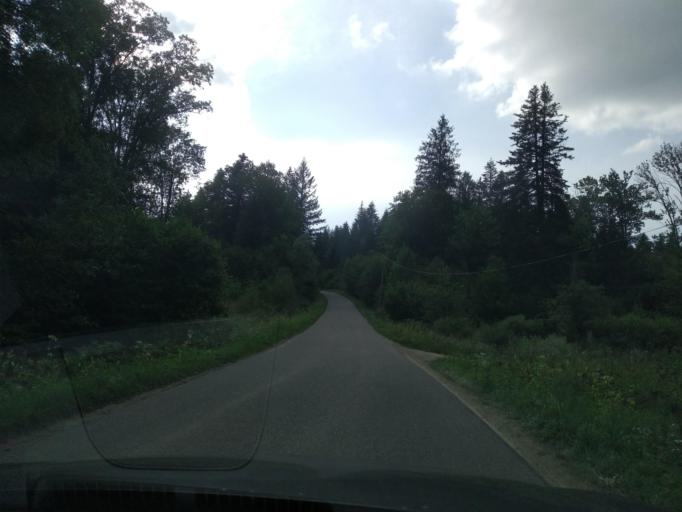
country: PL
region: Subcarpathian Voivodeship
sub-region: Powiat leski
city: Olszanica
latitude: 49.5178
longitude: 22.4564
